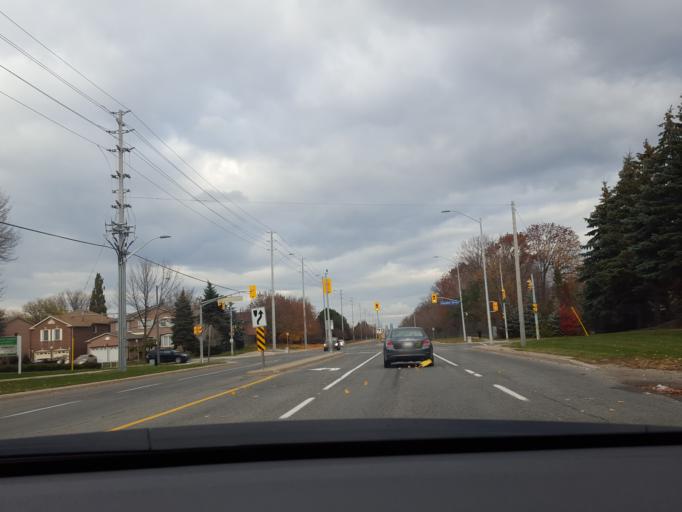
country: CA
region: Ontario
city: Mississauga
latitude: 43.5324
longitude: -79.7044
